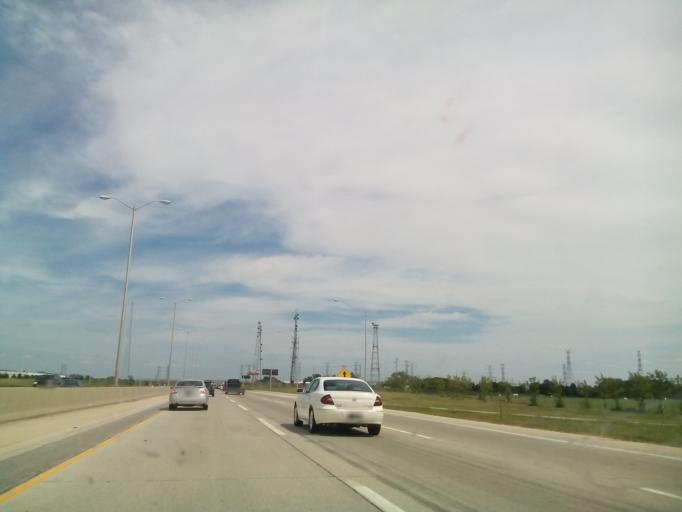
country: US
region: Illinois
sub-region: DuPage County
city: Warrenville
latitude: 41.8005
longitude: -88.2464
